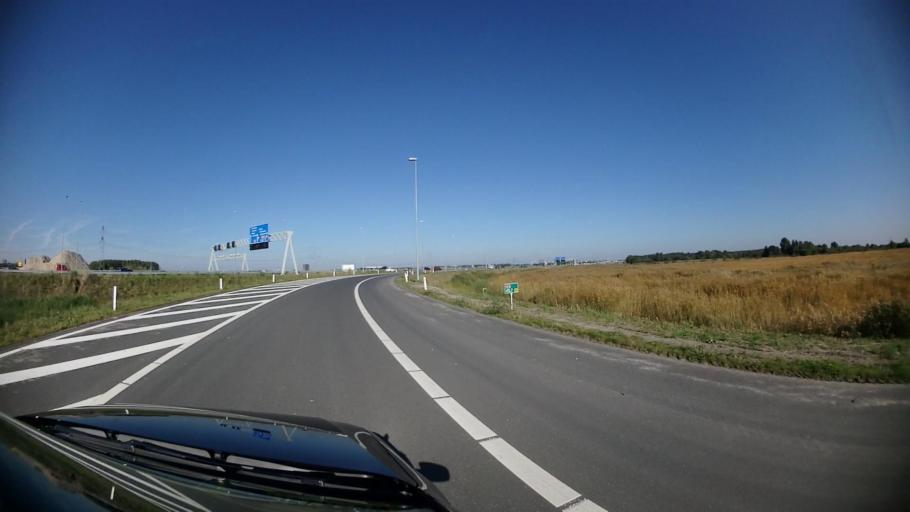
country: NL
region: North Holland
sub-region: Gemeente Naarden
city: Naarden
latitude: 52.3325
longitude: 5.1554
